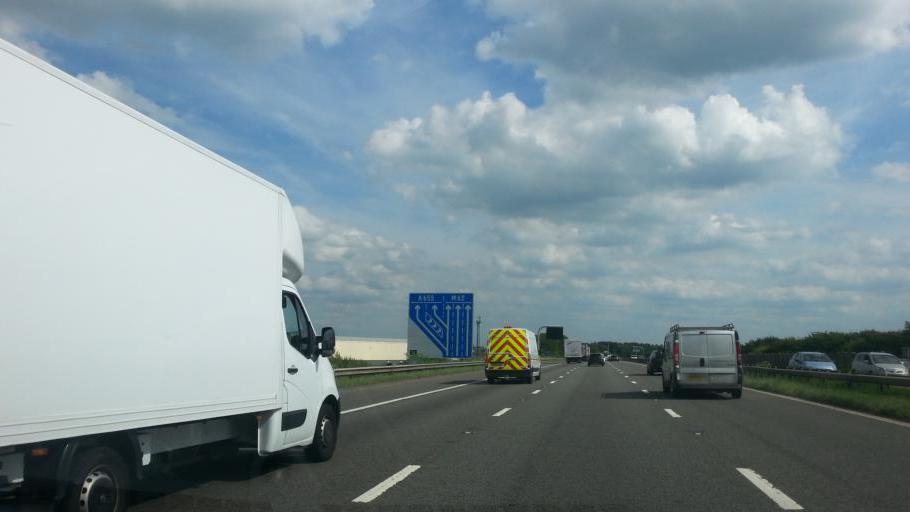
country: GB
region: England
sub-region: City and Borough of Wakefield
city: Normanton
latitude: 53.7165
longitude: -1.4219
